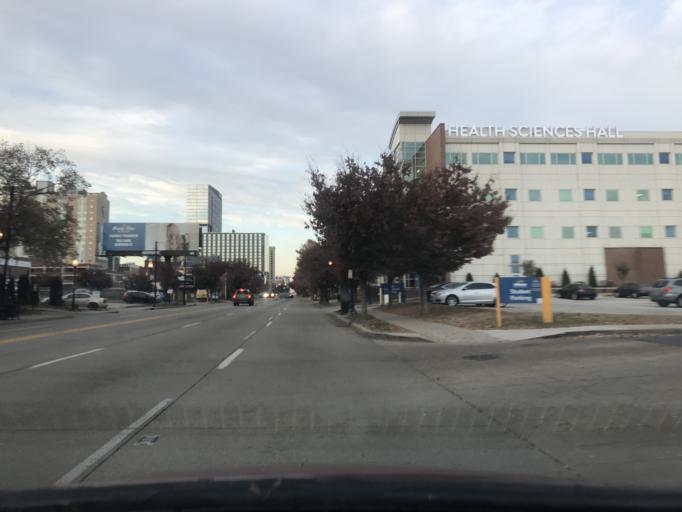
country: US
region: Kentucky
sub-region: Jefferson County
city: Louisville
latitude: 38.2472
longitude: -85.7547
